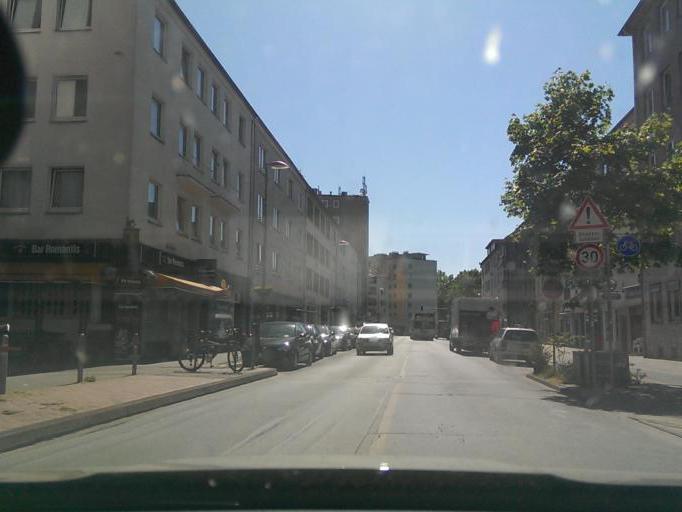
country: DE
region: Lower Saxony
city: Hannover
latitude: 52.3731
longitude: 9.7497
